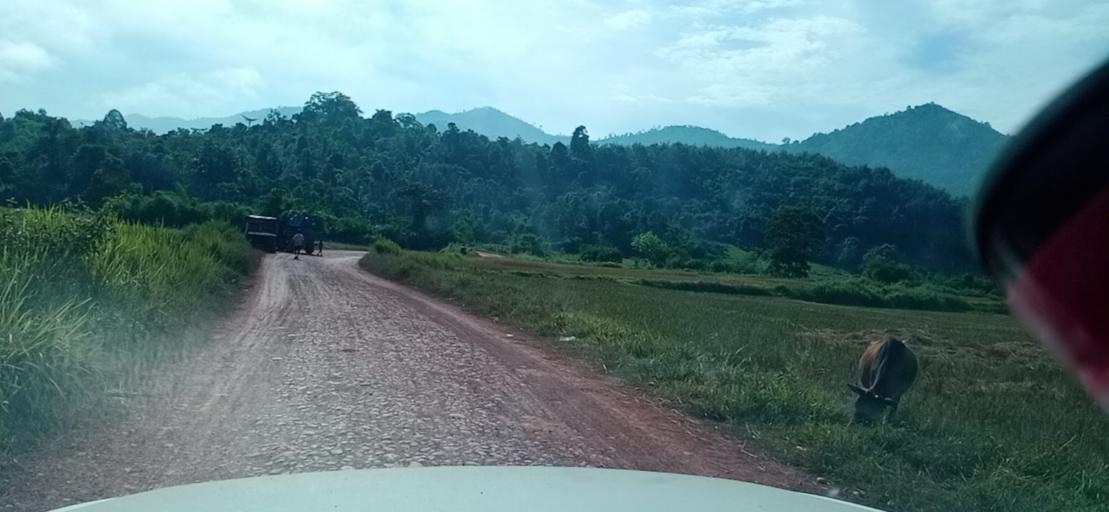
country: TH
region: Changwat Bueng Kan
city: Pak Khat
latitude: 18.6747
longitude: 103.1948
